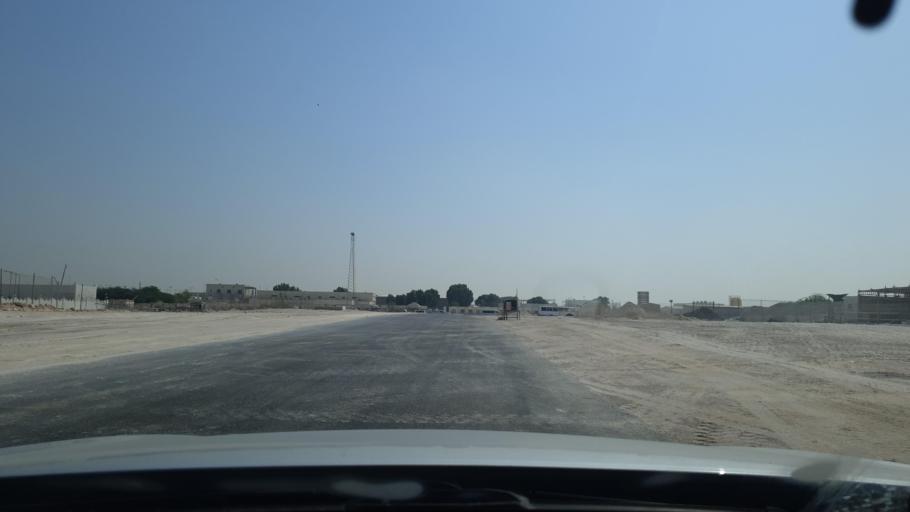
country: QA
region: Baladiyat ad Dawhah
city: Doha
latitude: 25.2299
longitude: 51.5199
